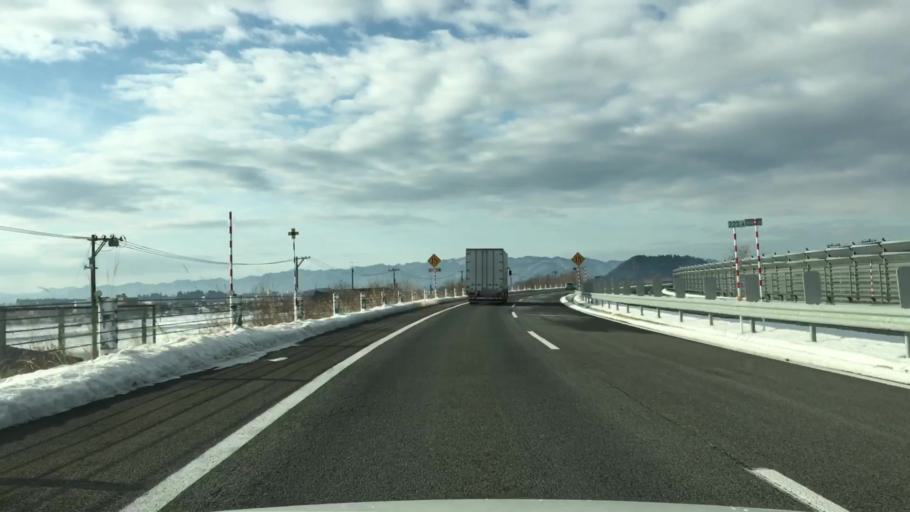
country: JP
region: Akita
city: Odate
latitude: 40.2925
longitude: 140.5516
